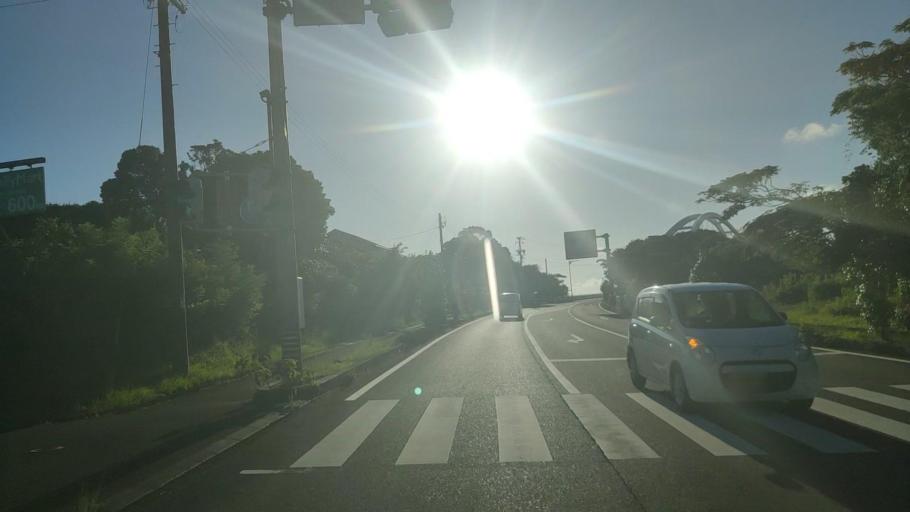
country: JP
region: Mie
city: Toba
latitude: 34.2638
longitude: 136.8175
